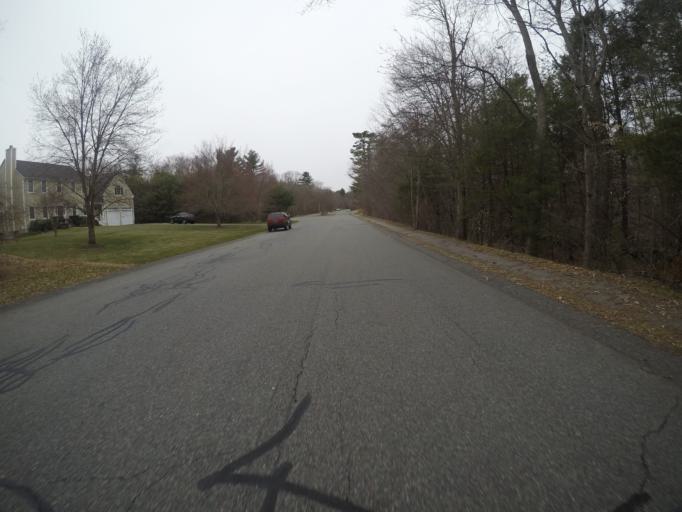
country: US
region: Massachusetts
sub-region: Bristol County
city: Easton
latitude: 42.0307
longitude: -71.1326
